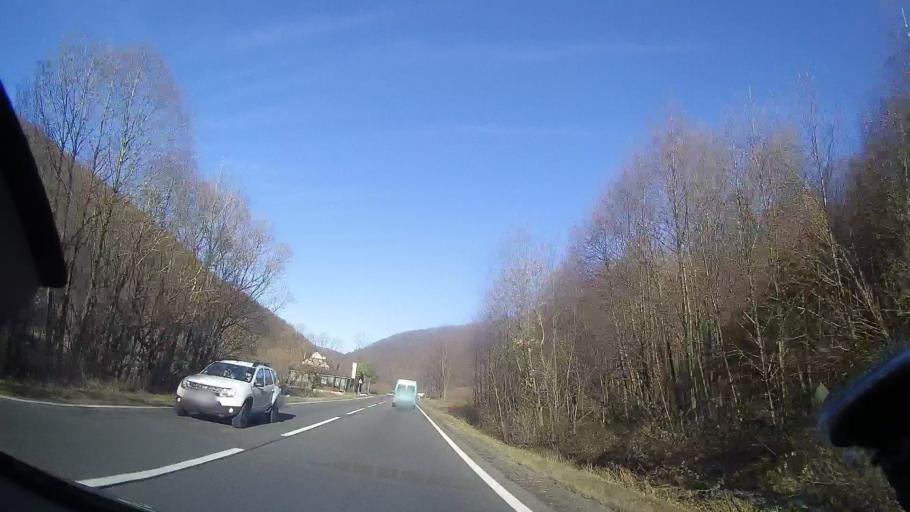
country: RO
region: Cluj
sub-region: Comuna Ciucea
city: Ciucea
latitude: 46.9378
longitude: 22.8201
